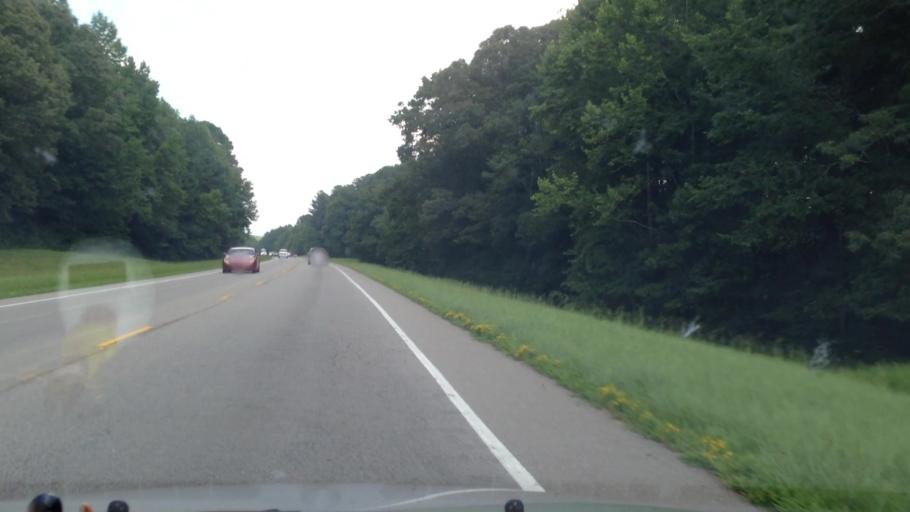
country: US
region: North Carolina
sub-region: Lee County
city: Broadway
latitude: 35.4400
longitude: -79.0935
